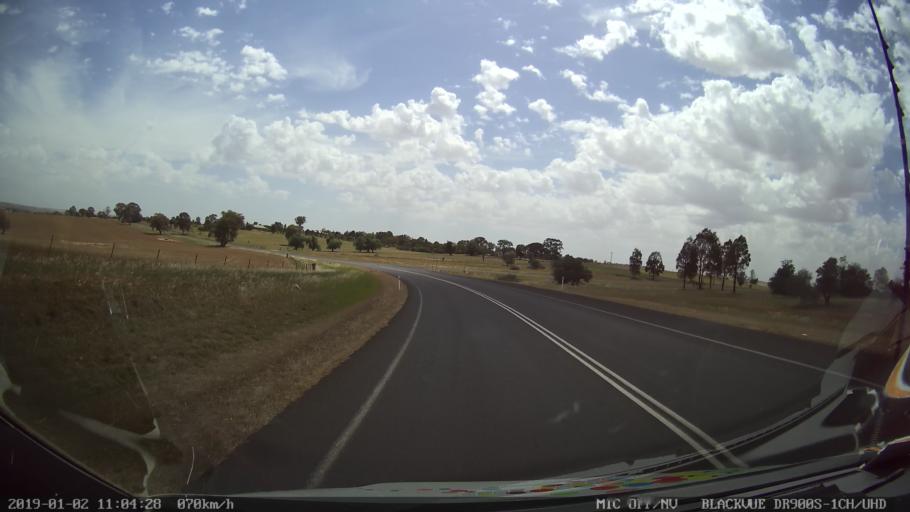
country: AU
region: New South Wales
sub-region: Young
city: Young
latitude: -34.5747
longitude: 148.3526
